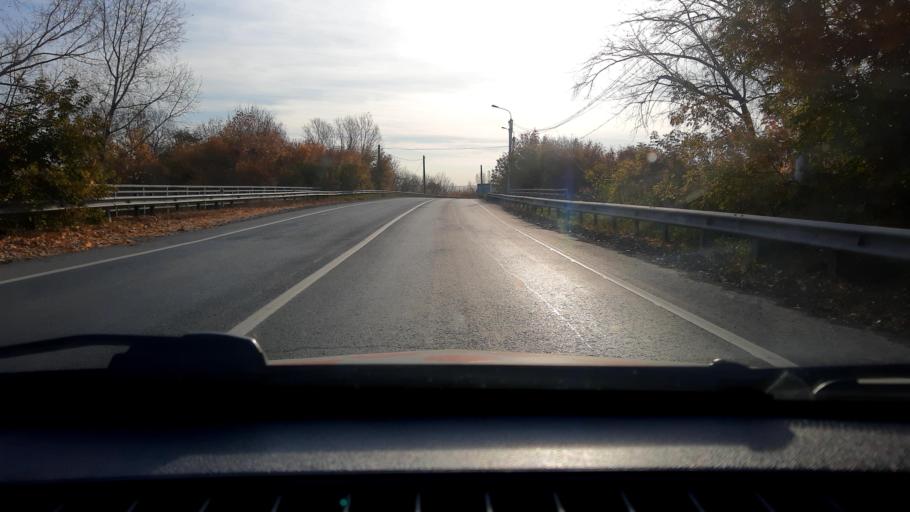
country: RU
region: Bashkortostan
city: Blagoveshchensk
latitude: 54.9153
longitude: 56.0794
